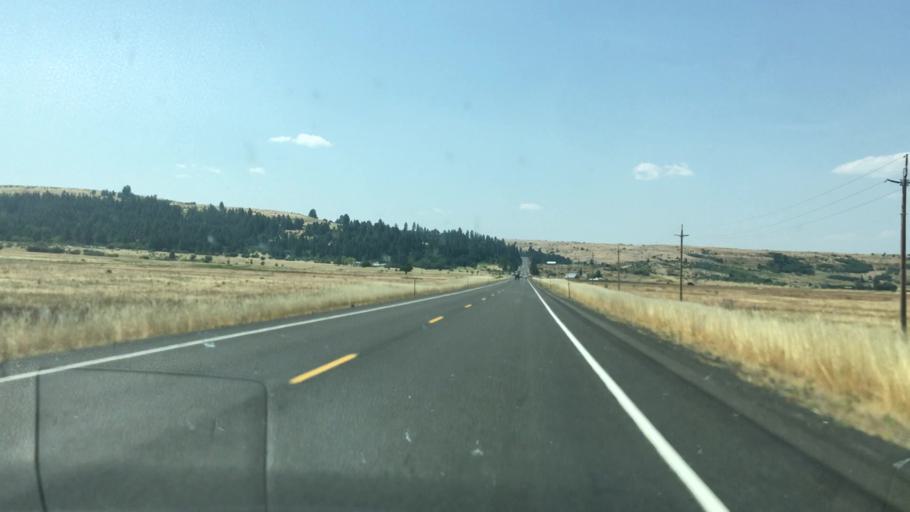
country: US
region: Idaho
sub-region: Idaho County
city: Grangeville
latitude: 45.8847
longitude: -116.2082
